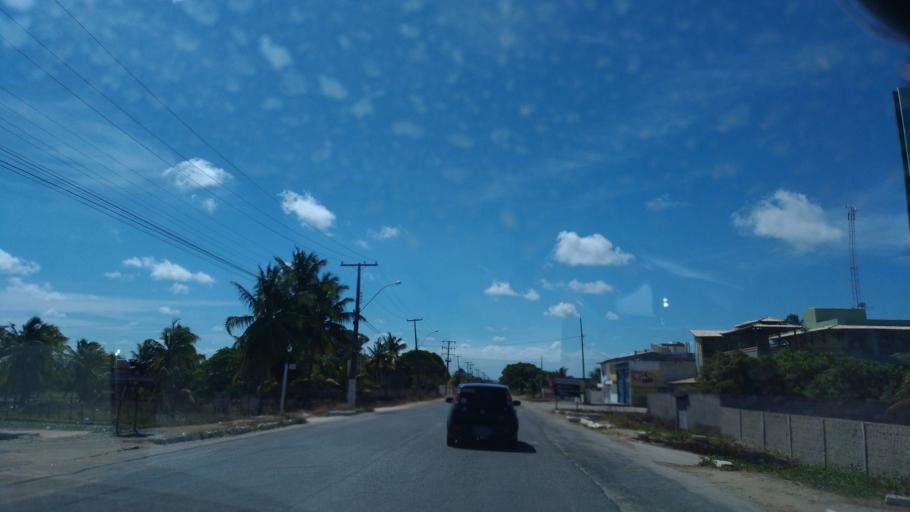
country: BR
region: Alagoas
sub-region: Marechal Deodoro
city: Marechal Deodoro
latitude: -9.7667
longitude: -35.8518
